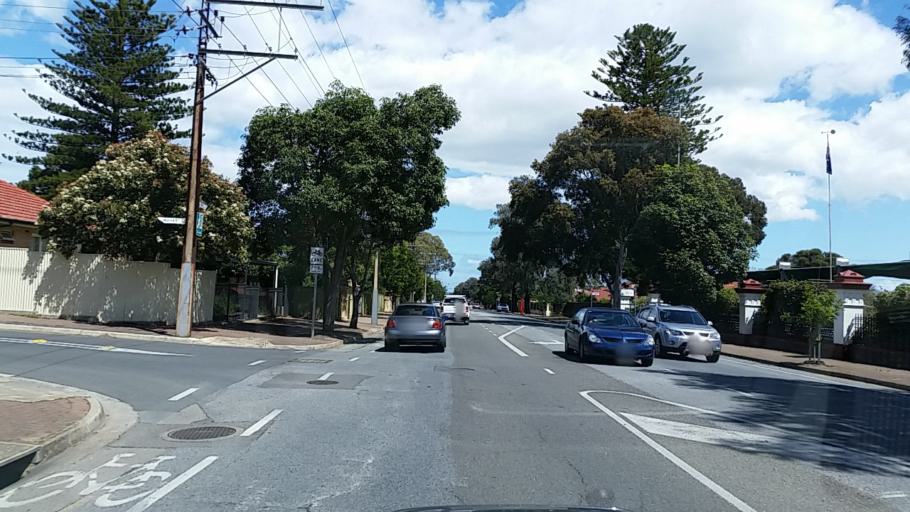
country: AU
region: South Australia
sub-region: Burnside
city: Kensington Gardens
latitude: -34.9137
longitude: 138.6631
